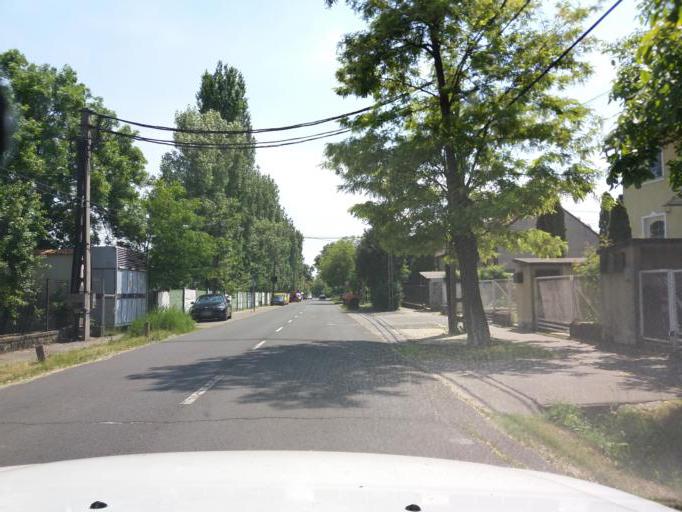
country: HU
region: Budapest
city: Budapest XXII. keruelet
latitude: 47.4491
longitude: 19.0241
